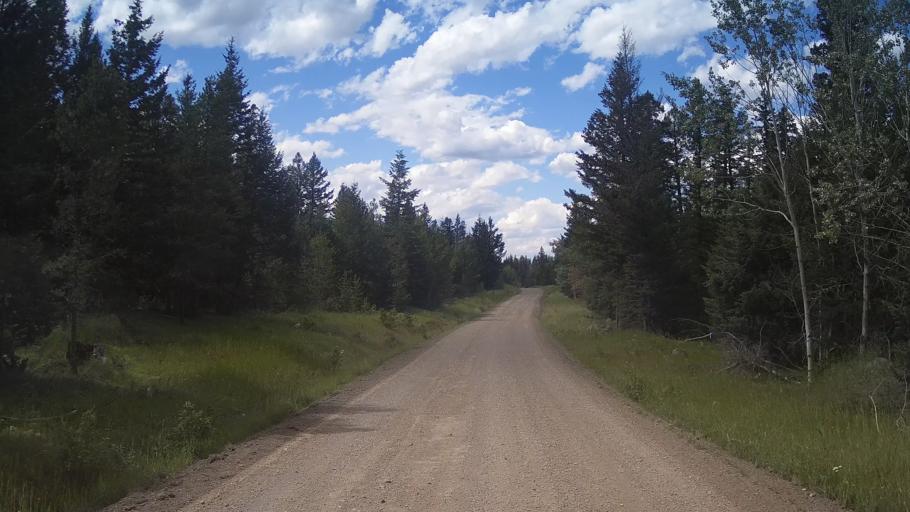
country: CA
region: British Columbia
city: Lillooet
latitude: 51.3218
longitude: -121.8658
